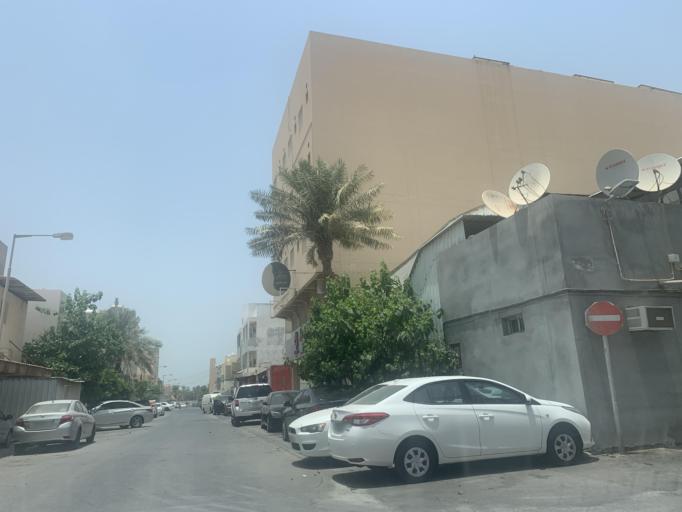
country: BH
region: Manama
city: Jidd Hafs
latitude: 26.2176
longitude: 50.4604
